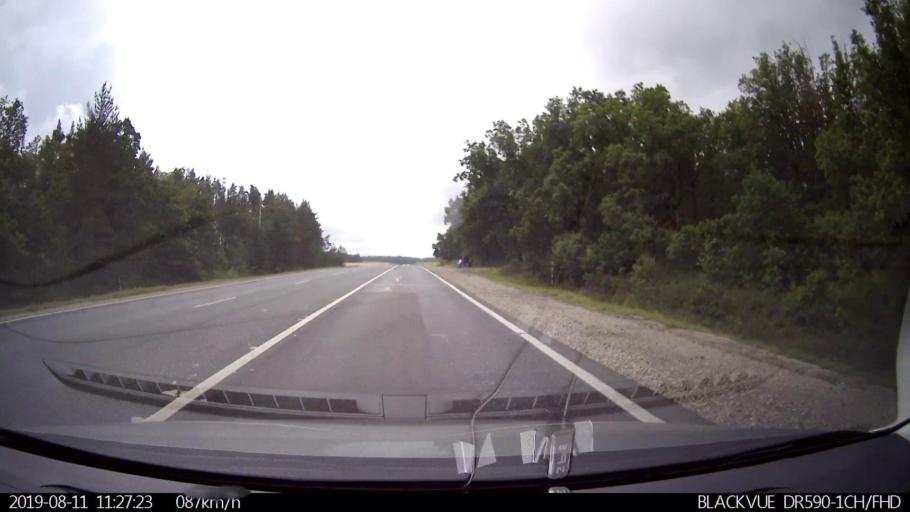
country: RU
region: Ulyanovsk
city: Krasnyy Gulyay
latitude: 54.0936
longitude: 48.2318
